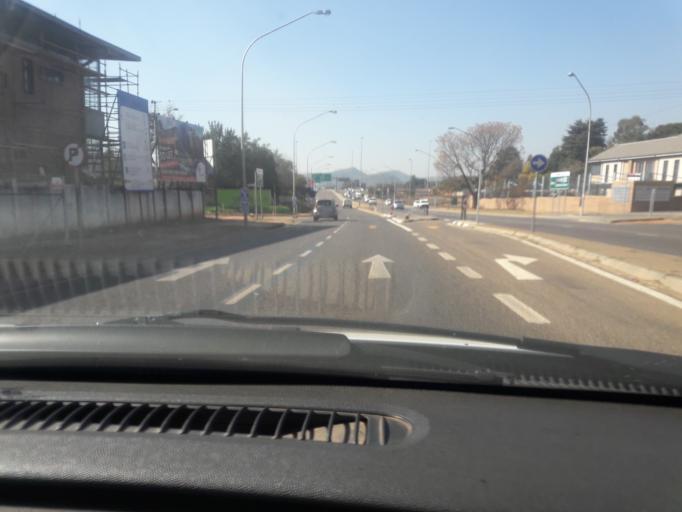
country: ZA
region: Gauteng
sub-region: City of Tshwane Metropolitan Municipality
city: Pretoria
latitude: -25.7654
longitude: 28.2708
